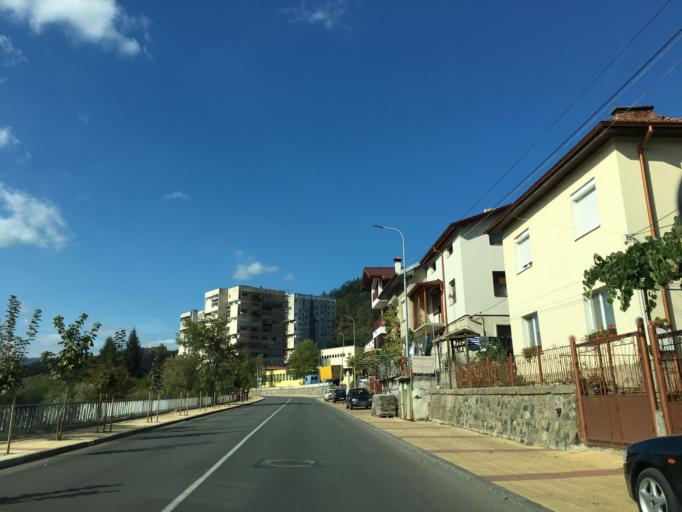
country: BG
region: Smolyan
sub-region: Obshtina Zlatograd
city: Zlatograd
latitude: 41.3858
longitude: 25.0897
